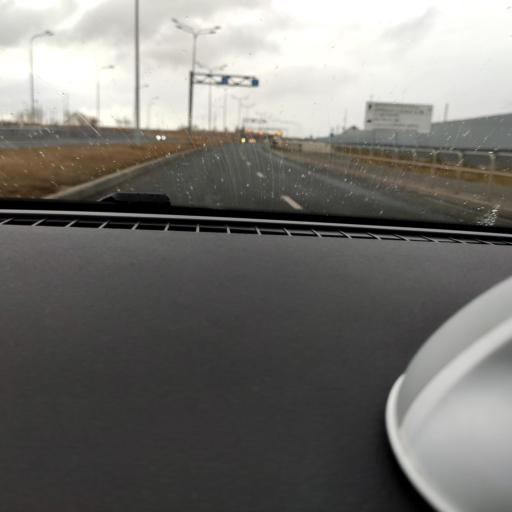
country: RU
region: Samara
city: Petra-Dubrava
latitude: 53.2808
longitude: 50.2443
